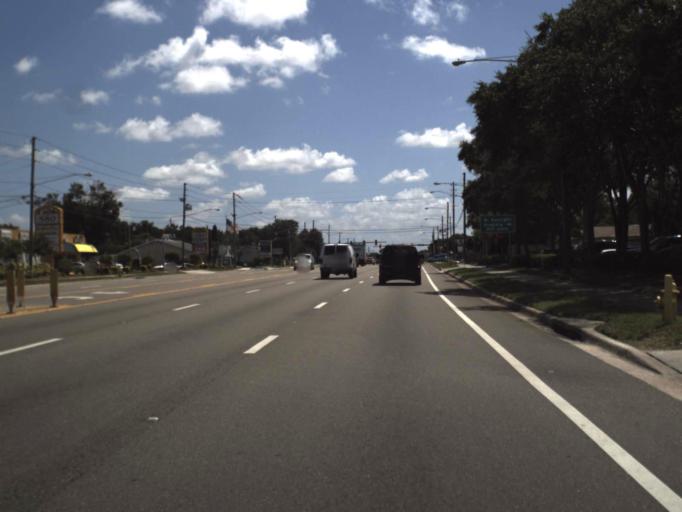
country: US
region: Florida
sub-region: Pinellas County
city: Dunedin
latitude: 28.0194
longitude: -82.7625
